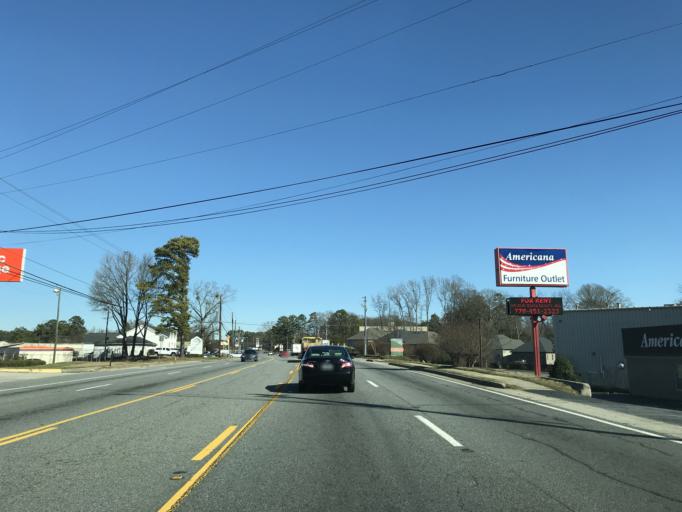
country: US
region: Georgia
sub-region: DeKalb County
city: Tucker
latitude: 33.8383
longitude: -84.2369
